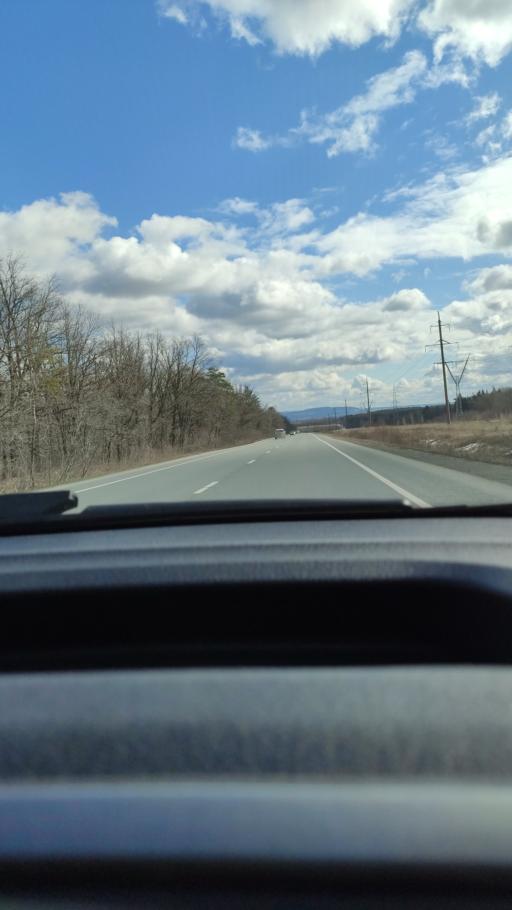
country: RU
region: Samara
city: Bogatyr'
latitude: 53.5027
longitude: 49.9471
